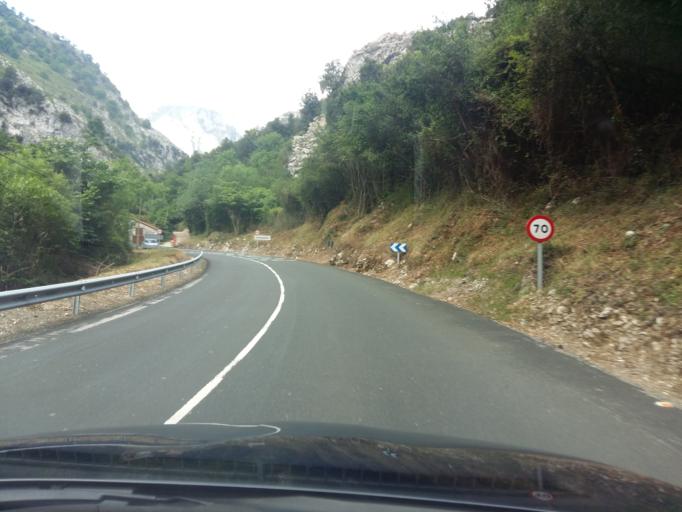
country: ES
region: Cantabria
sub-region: Provincia de Cantabria
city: Tresviso
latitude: 43.2929
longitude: -4.6141
